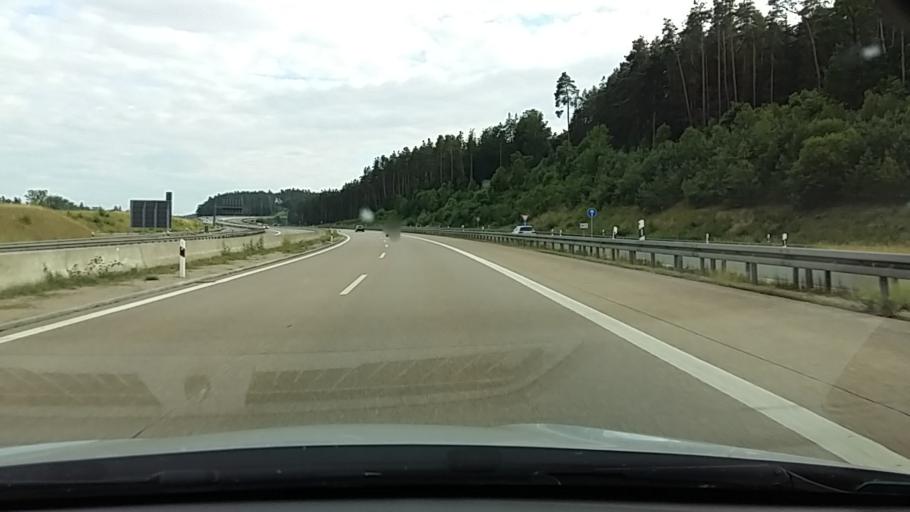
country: DE
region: Bavaria
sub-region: Upper Palatinate
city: Wernberg-Koblitz
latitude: 49.5171
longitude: 12.1627
